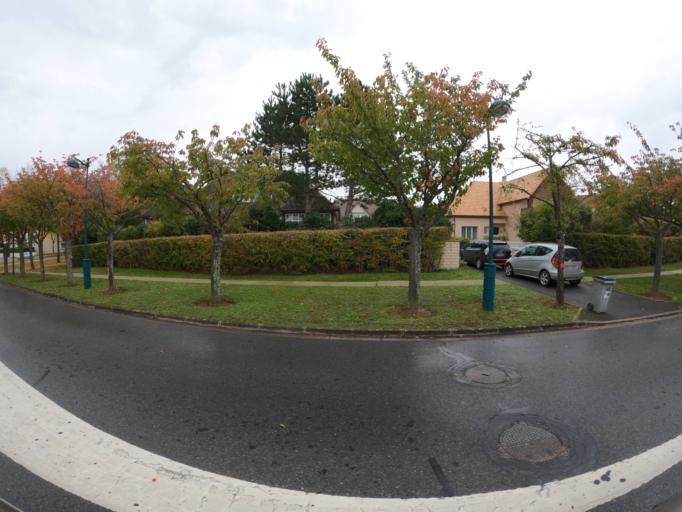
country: FR
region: Ile-de-France
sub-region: Departement de Seine-et-Marne
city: Magny-le-Hongre
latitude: 48.8592
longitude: 2.8103
